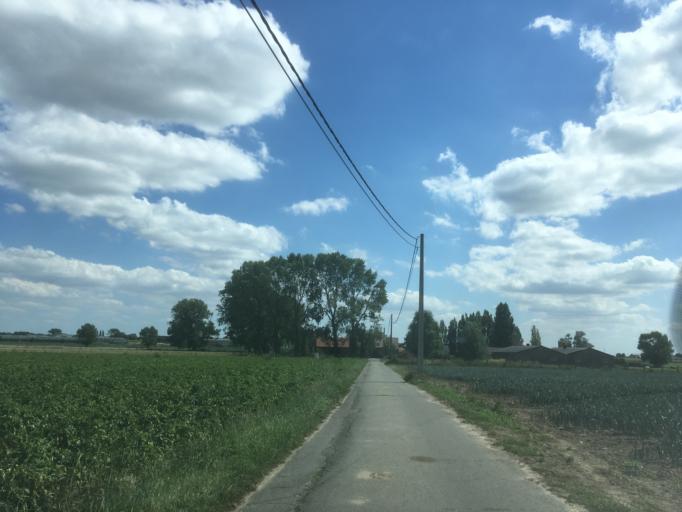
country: BE
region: Flanders
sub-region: Provincie West-Vlaanderen
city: Moorslede
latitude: 50.9323
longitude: 3.0435
